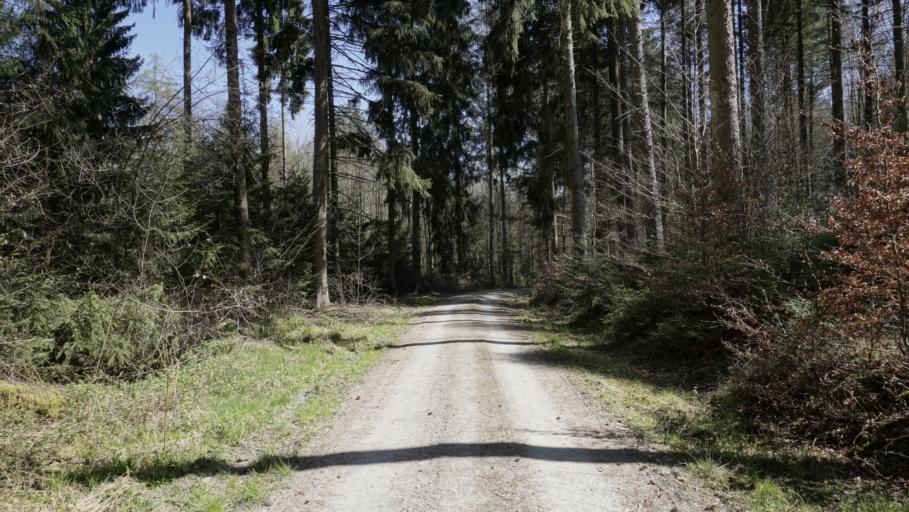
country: DE
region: Baden-Wuerttemberg
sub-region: Karlsruhe Region
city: Fahrenbach
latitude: 49.3986
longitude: 9.1733
